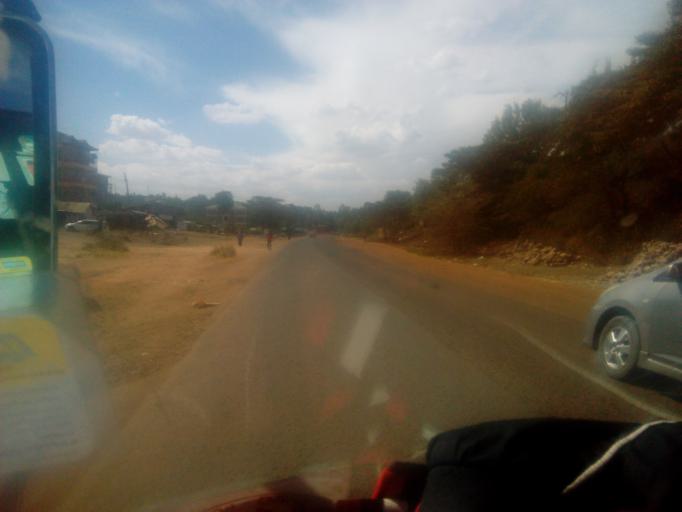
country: KE
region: Kiambu
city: Kikuyu
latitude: -1.2779
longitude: 36.6875
